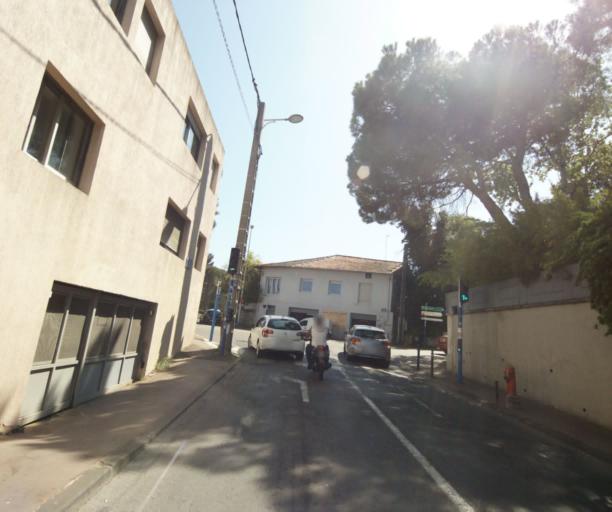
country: FR
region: Languedoc-Roussillon
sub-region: Departement de l'Herault
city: Montpellier
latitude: 43.5996
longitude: 3.8734
